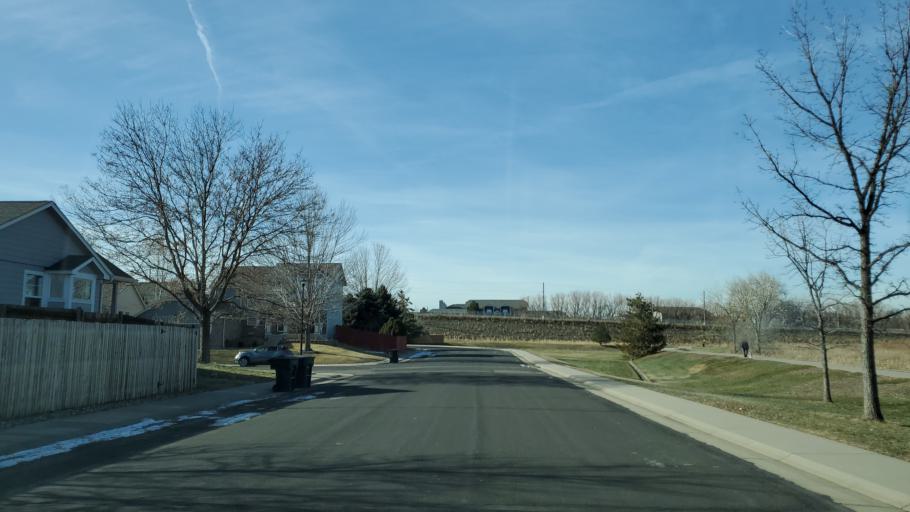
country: US
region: Colorado
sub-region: Adams County
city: Northglenn
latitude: 39.9169
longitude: -104.9564
